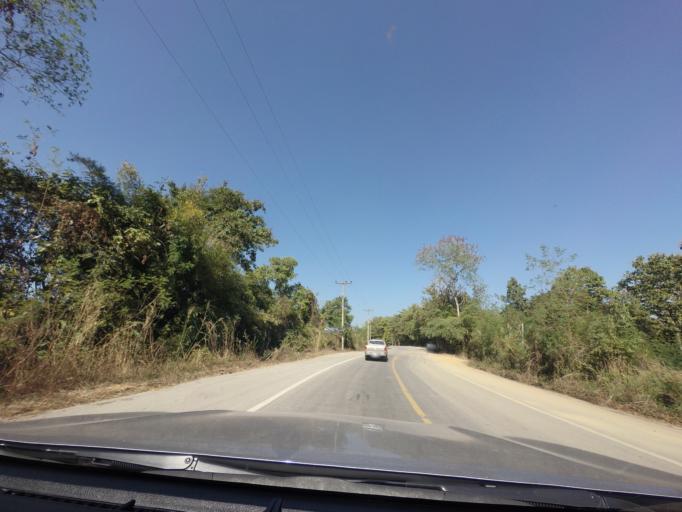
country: TH
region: Lampang
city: Chae Hom
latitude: 18.5253
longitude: 99.6433
